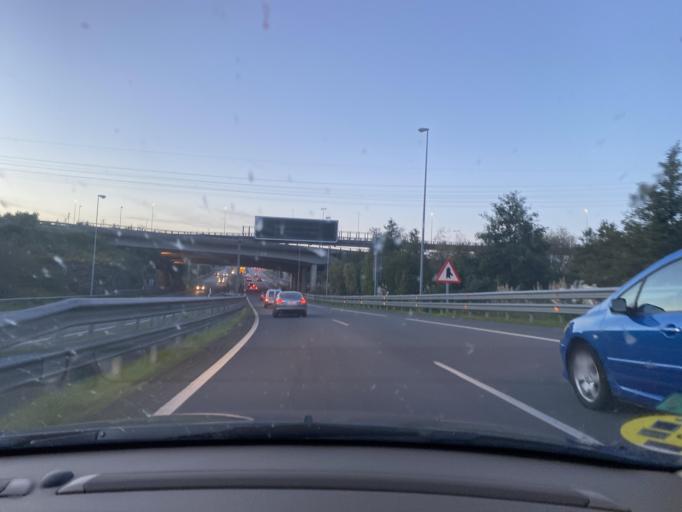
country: ES
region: Asturias
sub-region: Province of Asturias
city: Gijon
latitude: 43.5155
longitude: -5.6550
